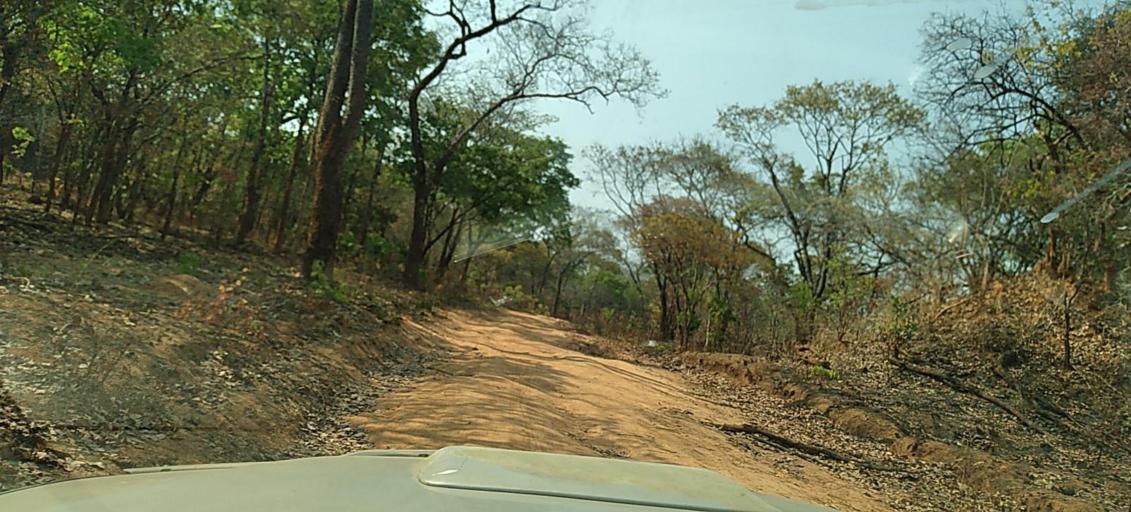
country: ZM
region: North-Western
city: Kasempa
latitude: -13.5328
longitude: 26.4082
